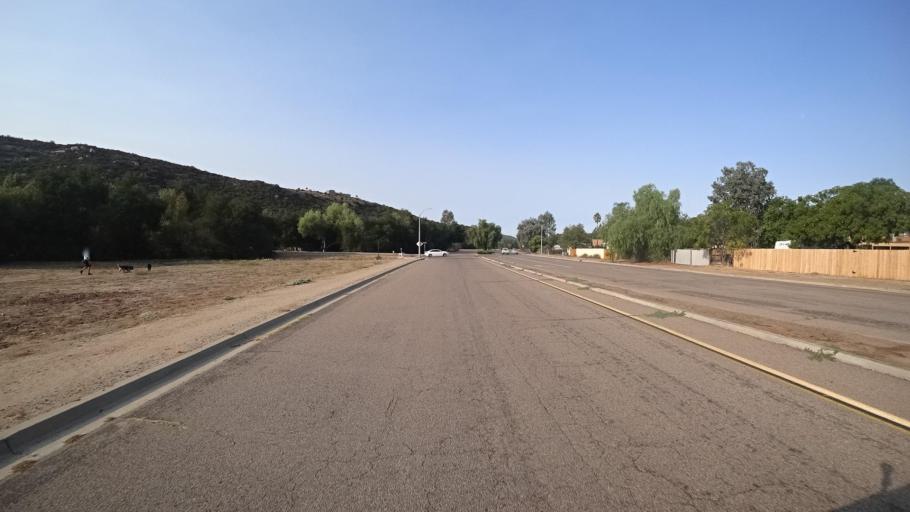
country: US
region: California
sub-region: San Diego County
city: San Diego Country Estates
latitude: 33.0112
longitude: -116.8089
